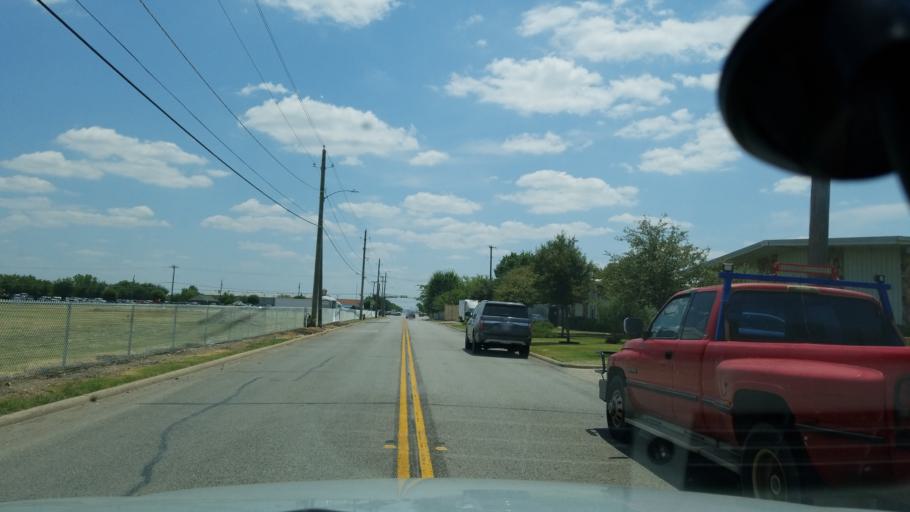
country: US
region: Texas
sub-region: Dallas County
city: Grand Prairie
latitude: 32.7515
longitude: -96.9707
